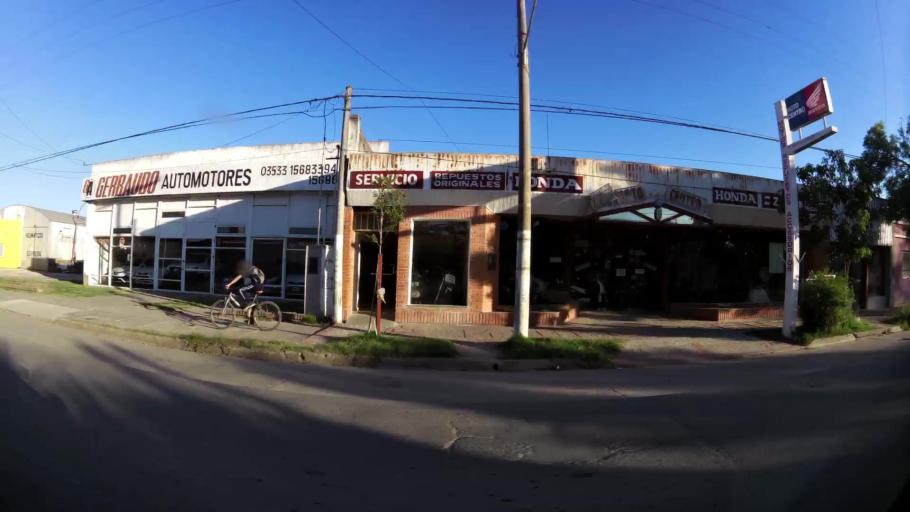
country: AR
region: Cordoba
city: Las Varillas
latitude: -31.8736
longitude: -62.7144
